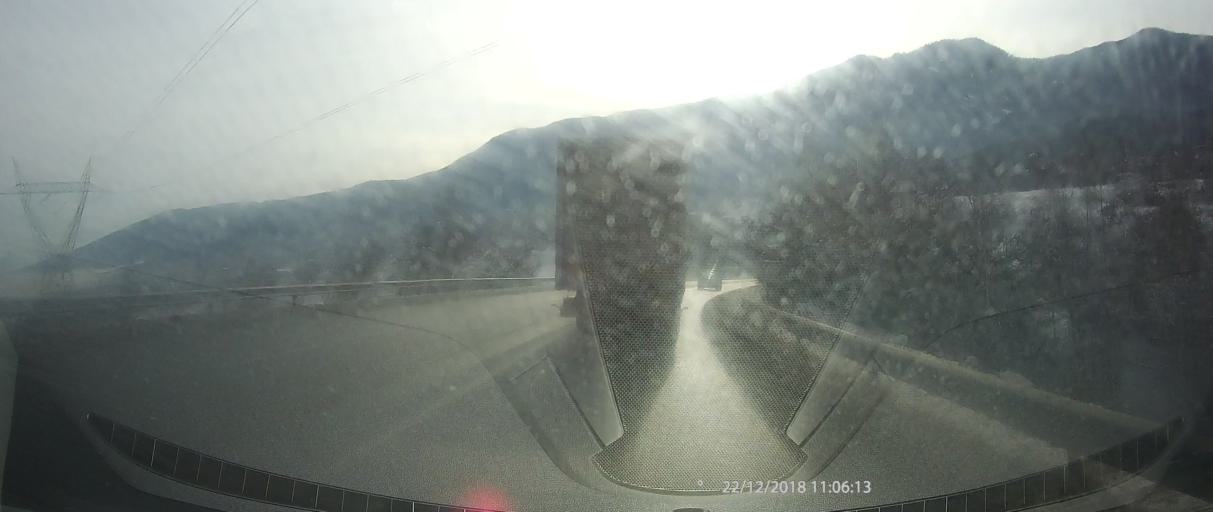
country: BG
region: Kyustendil
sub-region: Obshtina Kyustendil
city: Kyustendil
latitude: 42.2655
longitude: 22.5833
